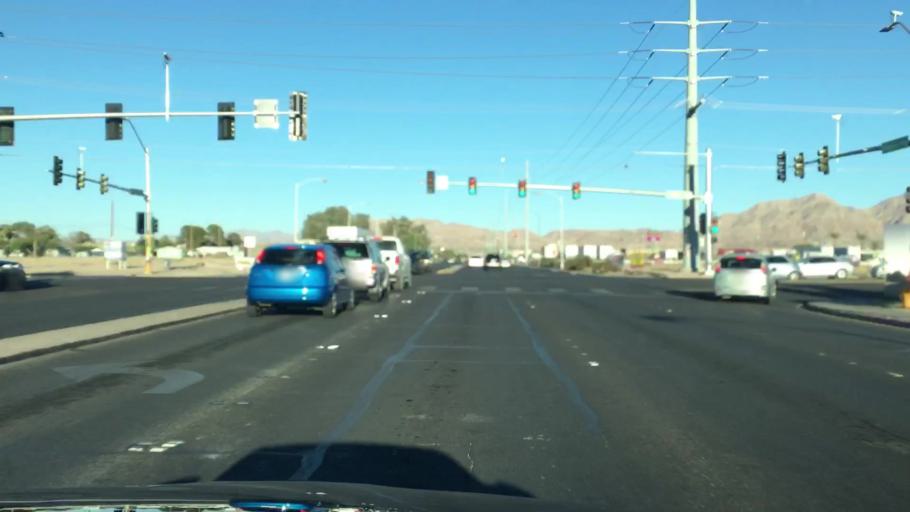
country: US
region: Nevada
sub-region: Clark County
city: North Las Vegas
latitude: 36.2176
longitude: -115.0990
